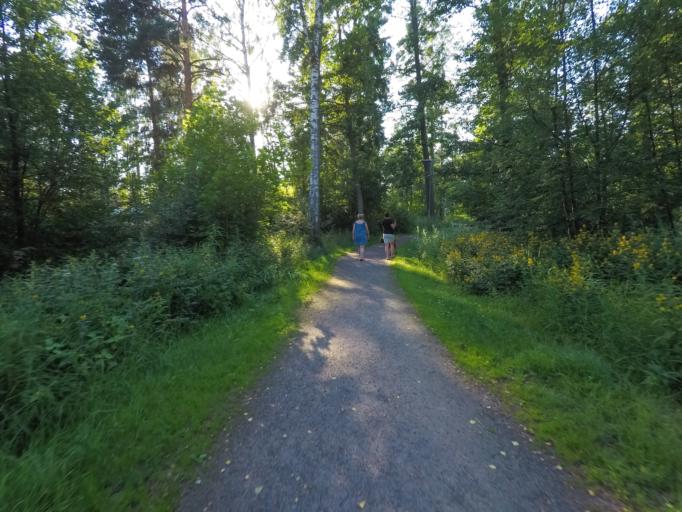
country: FI
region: Uusimaa
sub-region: Helsinki
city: Vantaa
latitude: 60.2146
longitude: 25.1077
